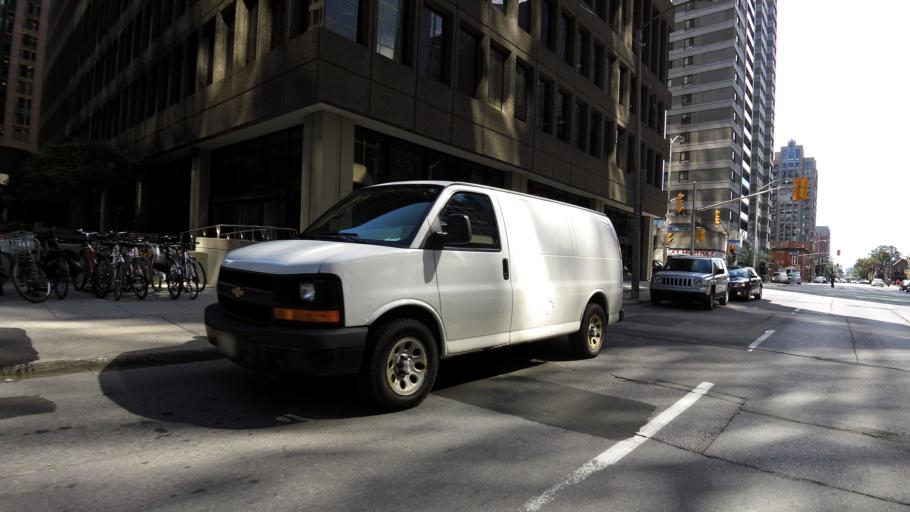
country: CA
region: Ontario
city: Ottawa
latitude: 45.4180
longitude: -75.7014
